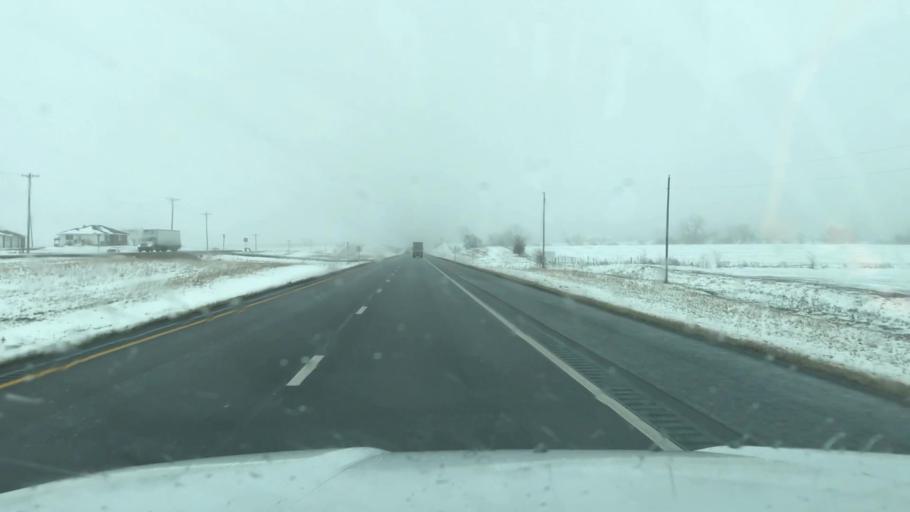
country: US
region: Missouri
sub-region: Clinton County
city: Gower
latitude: 39.7620
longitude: -94.5190
